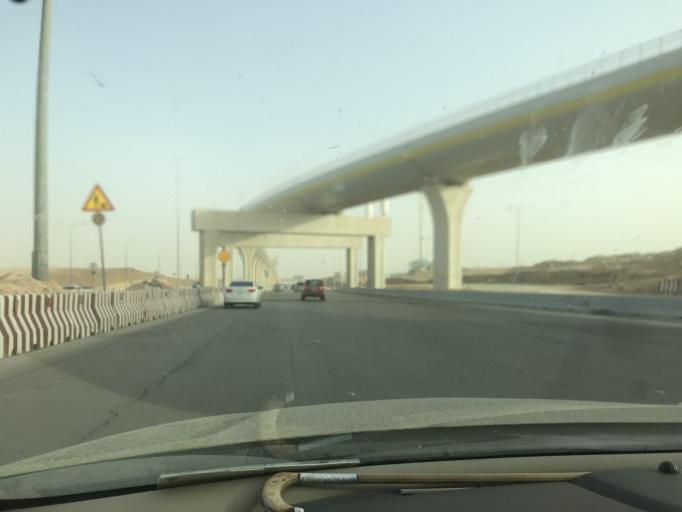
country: SA
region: Ar Riyad
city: Riyadh
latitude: 24.8742
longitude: 46.6948
